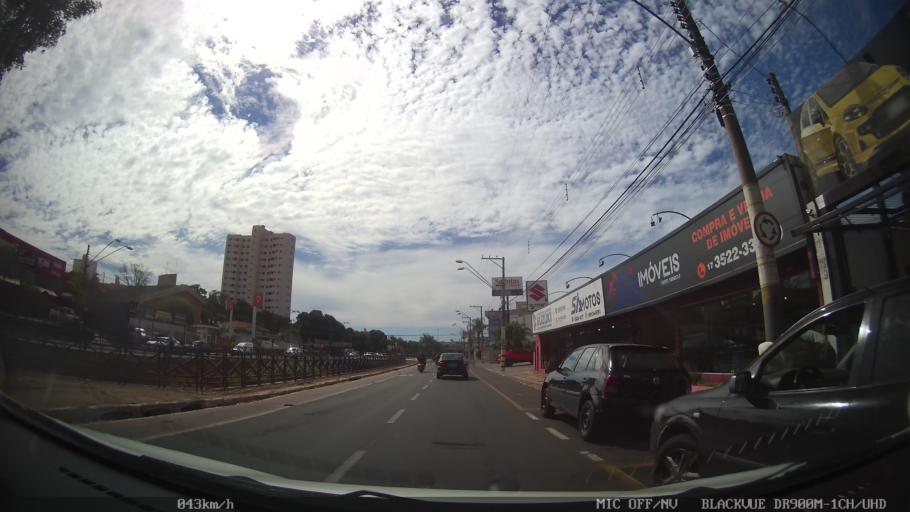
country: BR
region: Sao Paulo
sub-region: Catanduva
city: Catanduva
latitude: -21.1440
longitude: -48.9714
